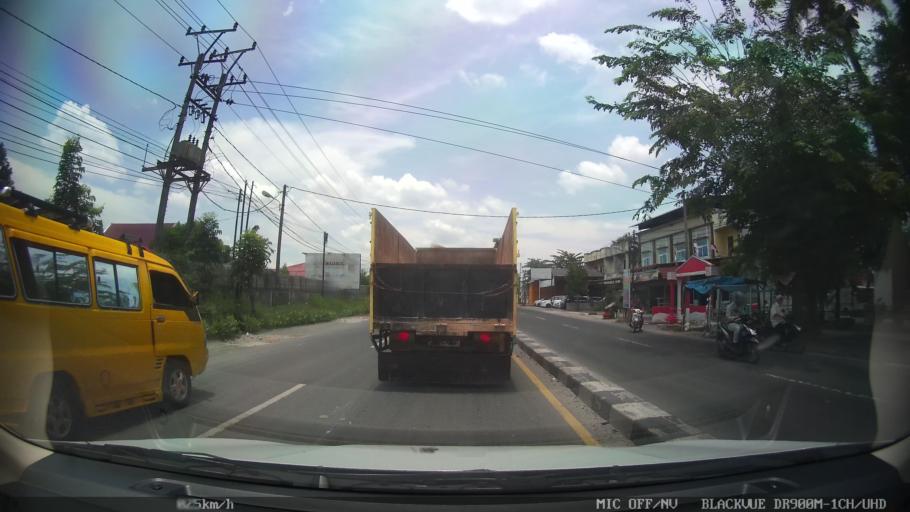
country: ID
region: North Sumatra
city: Binjai
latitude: 3.6009
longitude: 98.5478
